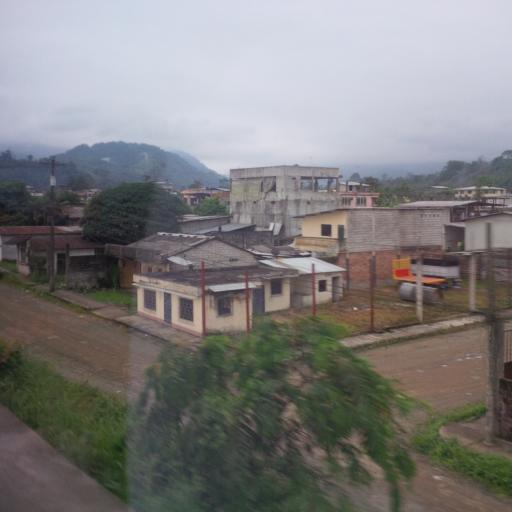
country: EC
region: Chimborazo
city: Alausi
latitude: -2.2102
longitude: -79.1355
